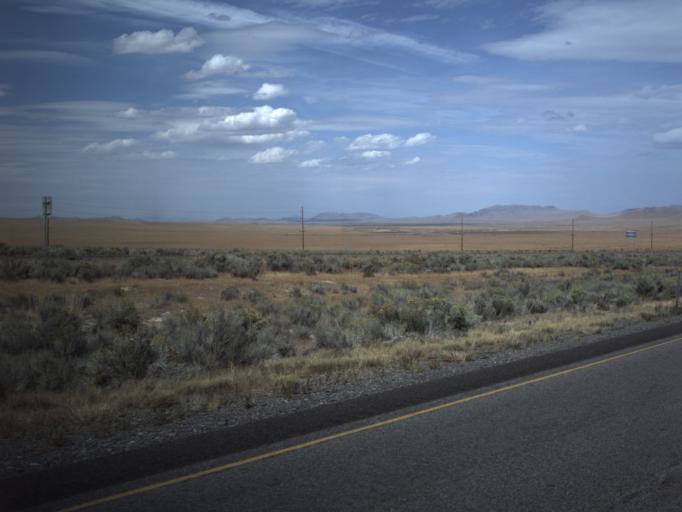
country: US
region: Utah
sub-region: Tooele County
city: Grantsville
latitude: 40.7698
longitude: -112.9817
